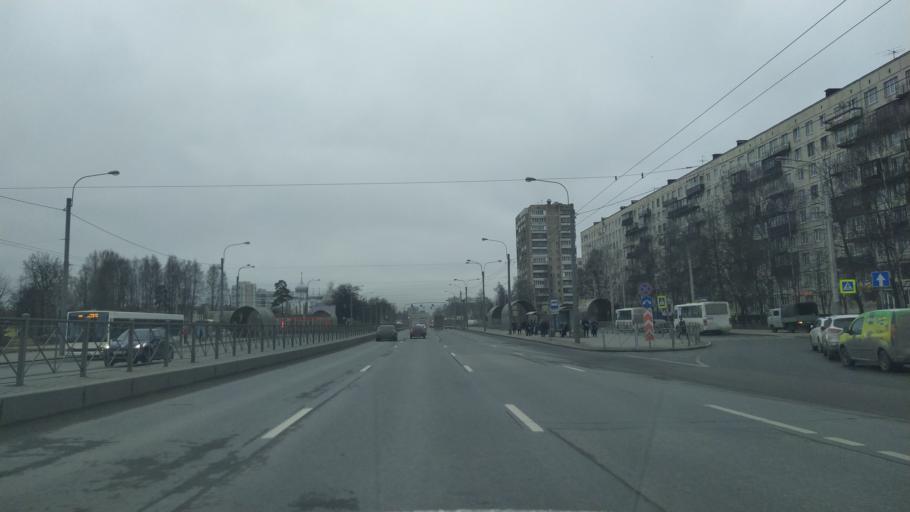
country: RU
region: Leningrad
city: Kalininskiy
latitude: 59.9858
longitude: 30.4271
